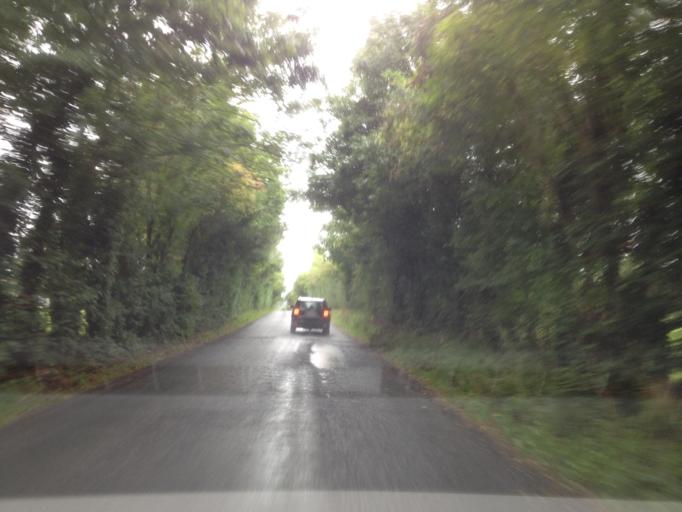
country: FR
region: Lower Normandy
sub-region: Departement du Calvados
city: Saint-Vigor-le-Grand
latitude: 49.3004
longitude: -0.6951
